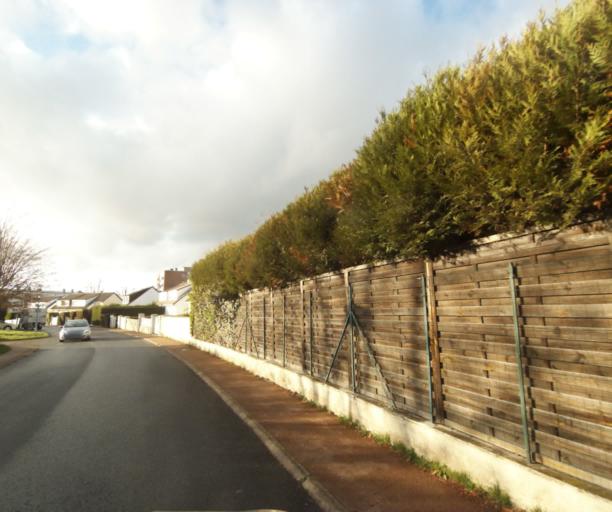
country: FR
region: Ile-de-France
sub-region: Departement des Yvelines
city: Meulan-en-Yvelines
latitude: 49.0115
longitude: 1.9209
